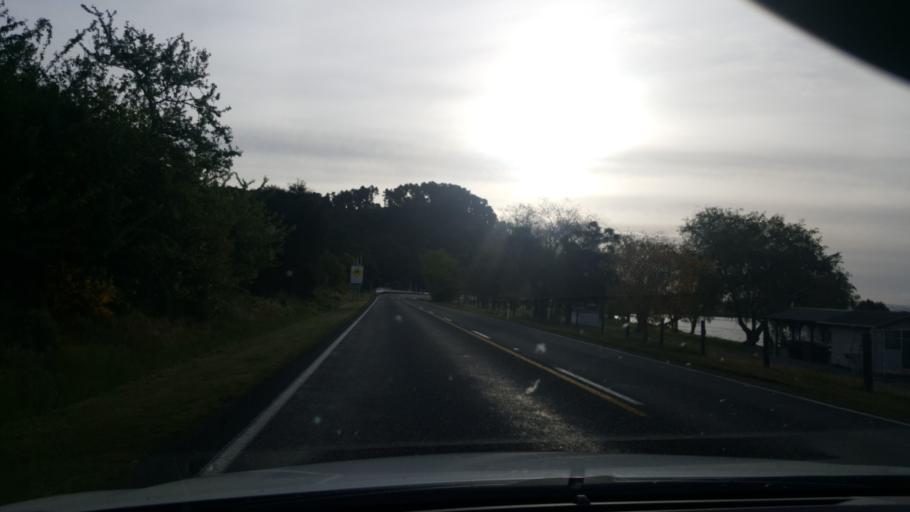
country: NZ
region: Waikato
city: Turangi
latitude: -38.8866
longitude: 175.9622
